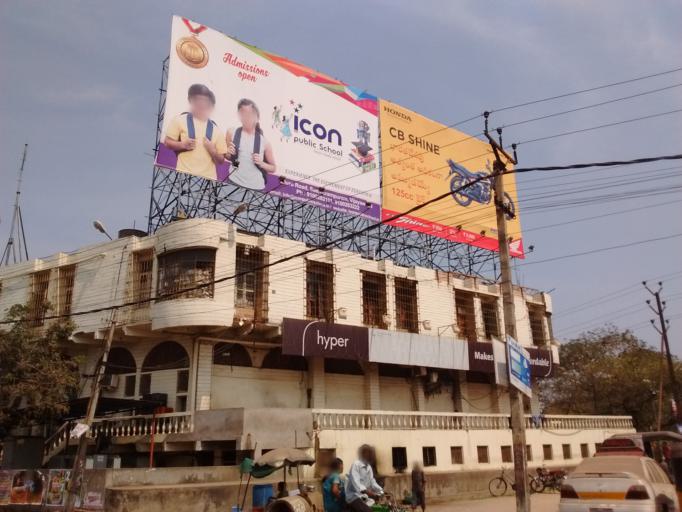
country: IN
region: Andhra Pradesh
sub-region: Krishna
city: Yanamalakuduru
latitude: 16.5060
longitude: 80.6615
